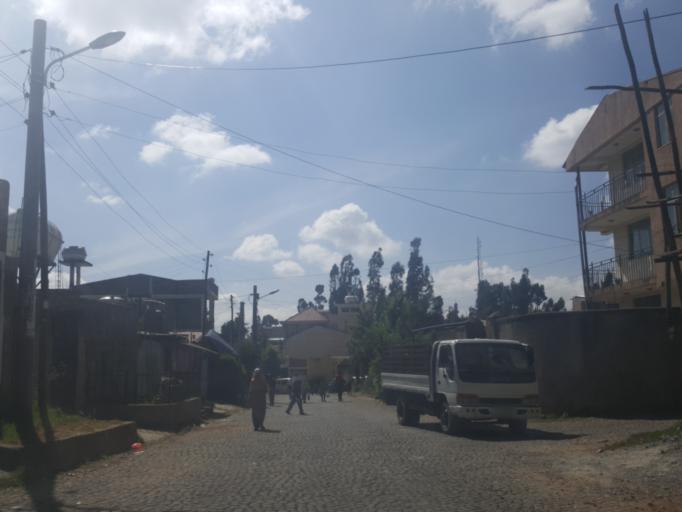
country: ET
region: Adis Abeba
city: Addis Ababa
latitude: 9.0649
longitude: 38.7264
